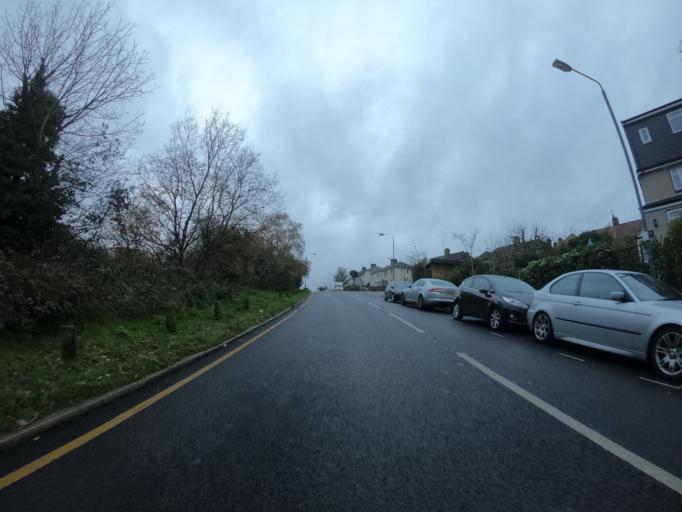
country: GB
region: England
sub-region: Greater London
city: Woolwich
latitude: 51.4859
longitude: 0.0412
